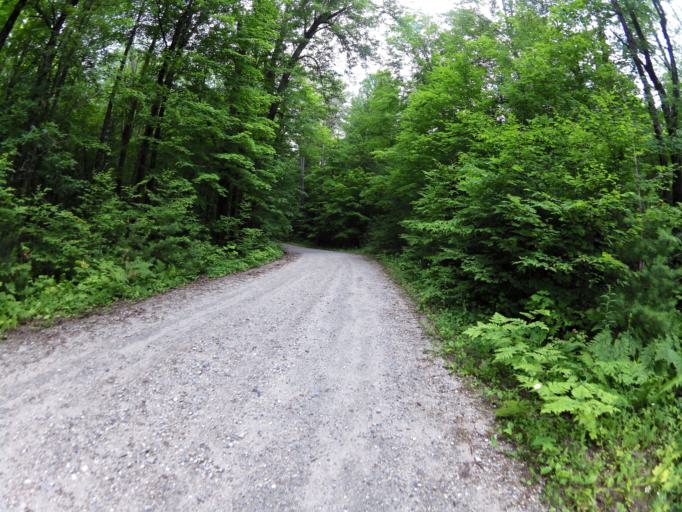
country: CA
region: Ontario
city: Perth
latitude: 45.0274
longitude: -76.5635
